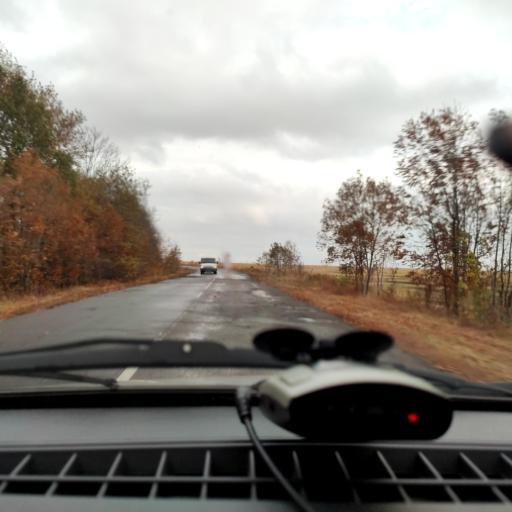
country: RU
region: Voronezj
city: Uryv-Pokrovka
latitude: 51.2409
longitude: 38.9816
